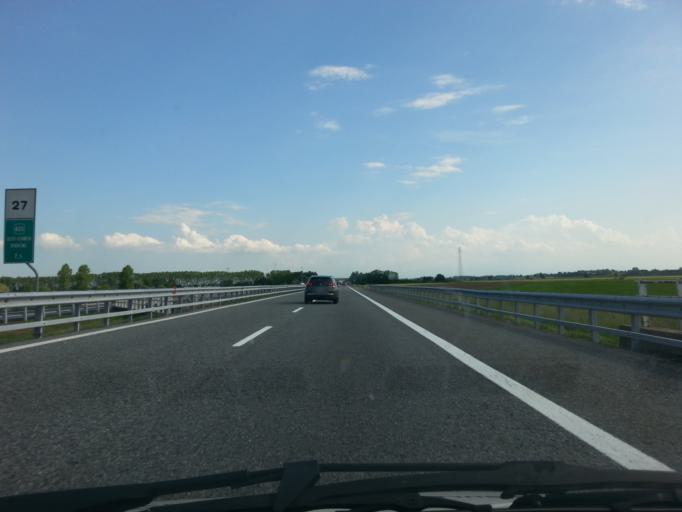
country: IT
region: Piedmont
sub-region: Provincia di Cuneo
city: Sommariva del Bosco
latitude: 44.7291
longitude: 7.7558
